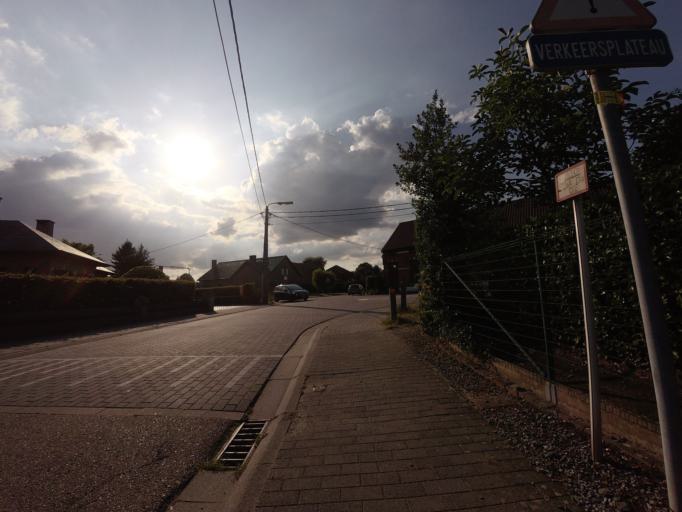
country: BE
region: Flanders
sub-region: Provincie Vlaams-Brabant
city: Boortmeerbeek
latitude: 50.9793
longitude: 4.5648
